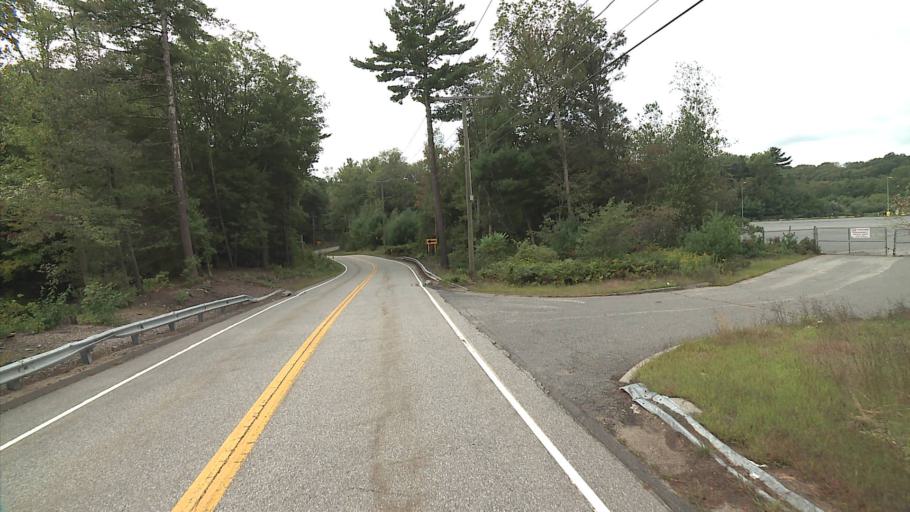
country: US
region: Connecticut
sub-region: Tolland County
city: Stafford Springs
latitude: 41.9155
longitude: -72.2612
